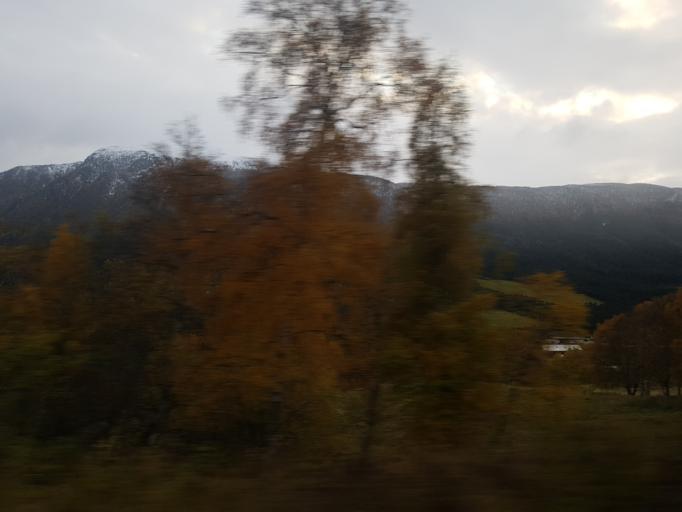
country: NO
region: Oppland
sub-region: Dovre
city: Dombas
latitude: 62.0246
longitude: 9.1848
